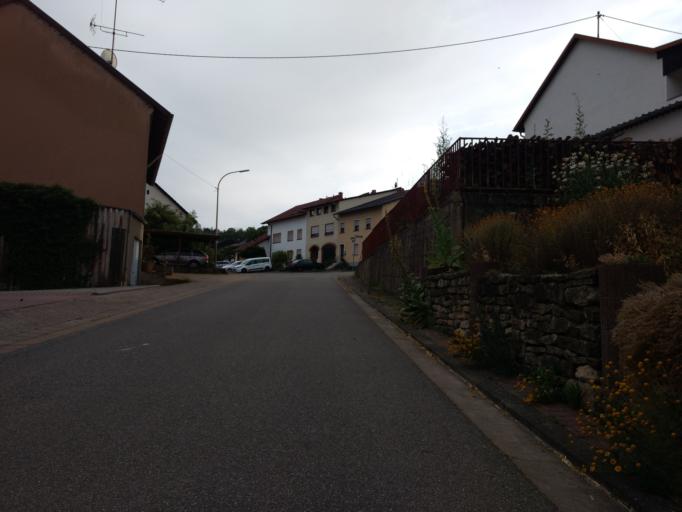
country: FR
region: Lorraine
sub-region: Departement de la Moselle
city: Bouzonville
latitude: 49.3223
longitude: 6.6015
